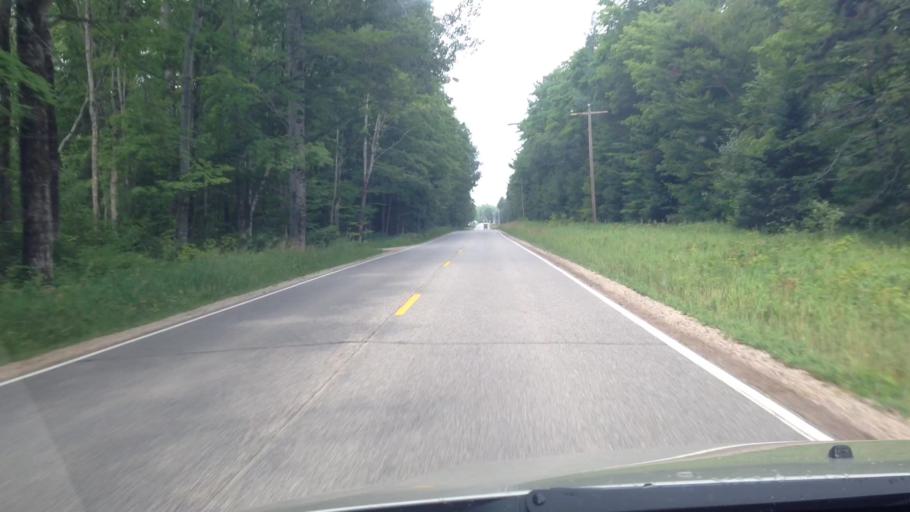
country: US
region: Michigan
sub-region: Mackinac County
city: Saint Ignace
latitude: 46.0569
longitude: -85.1422
